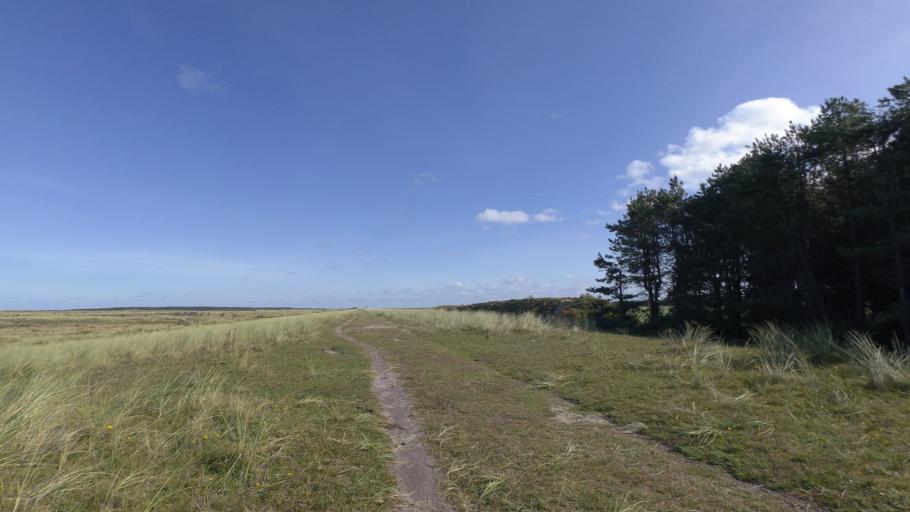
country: NL
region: Friesland
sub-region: Gemeente Ameland
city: Nes
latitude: 53.4525
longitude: 5.7165
